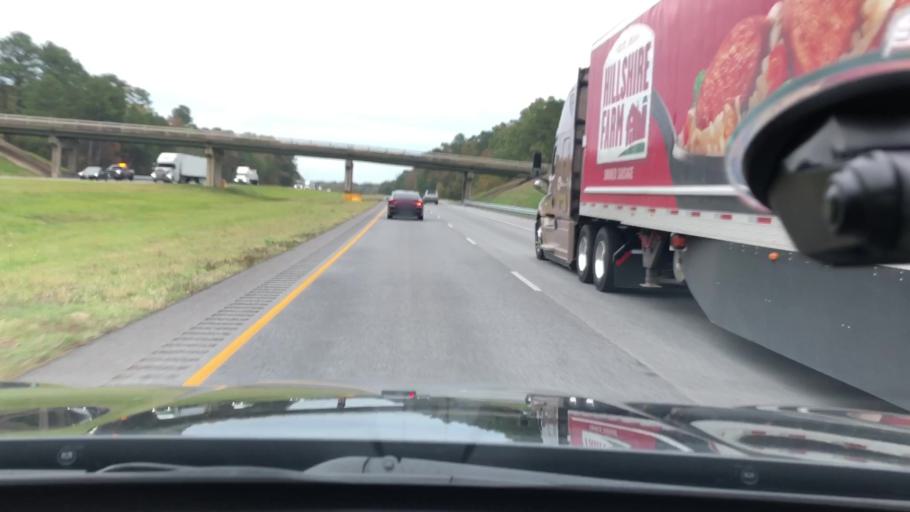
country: US
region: Arkansas
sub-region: Hempstead County
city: Hope
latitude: 33.6296
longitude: -93.7292
